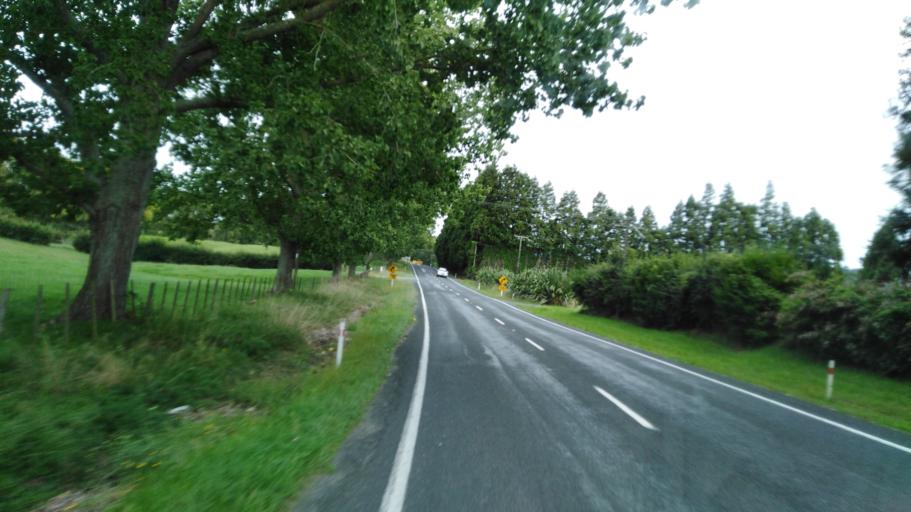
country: NZ
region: Waikato
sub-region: Hauraki District
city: Waihi
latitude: -37.4129
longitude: 175.8777
